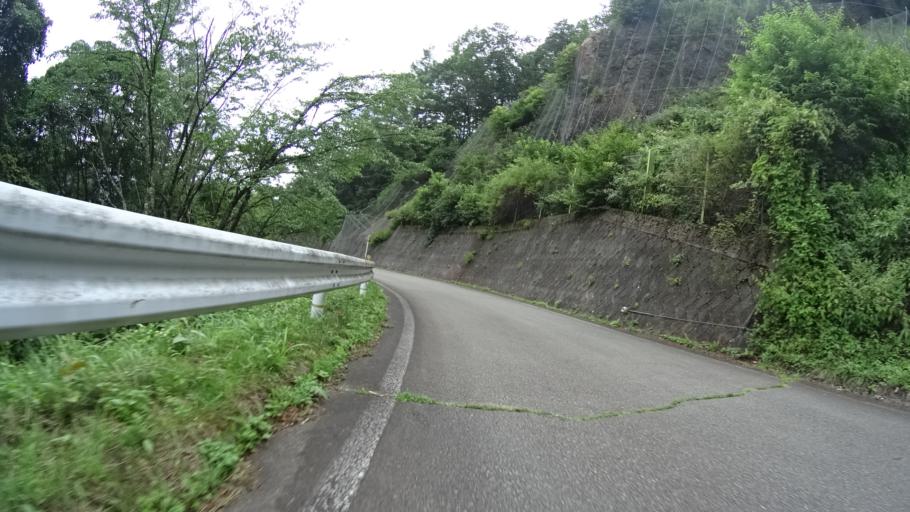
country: JP
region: Nagano
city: Saku
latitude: 36.0658
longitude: 138.6415
